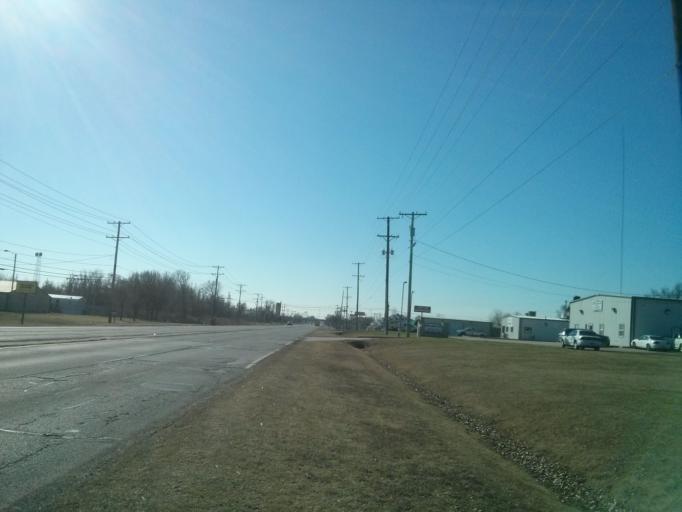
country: US
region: Oklahoma
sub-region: Tulsa County
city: Owasso
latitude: 36.1729
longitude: -95.8689
